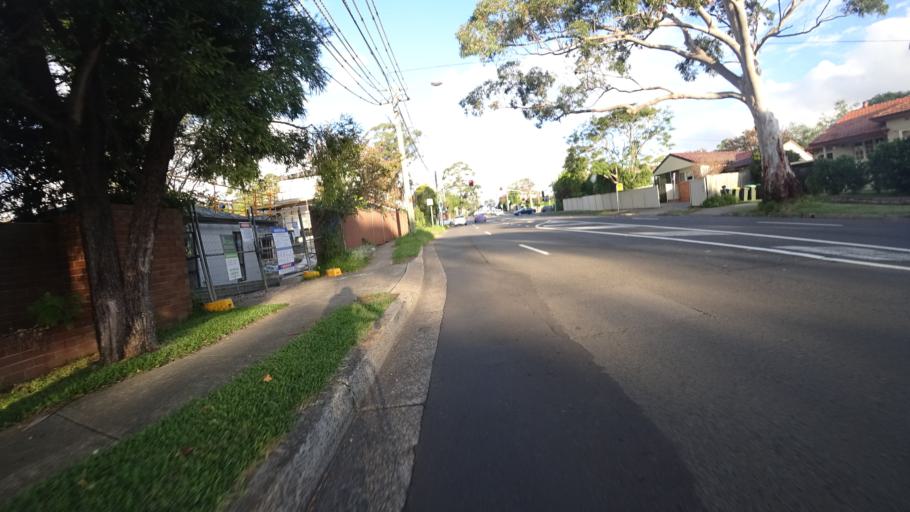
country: AU
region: New South Wales
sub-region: Lane Cove
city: Lane Cove
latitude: -33.8192
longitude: 151.1644
